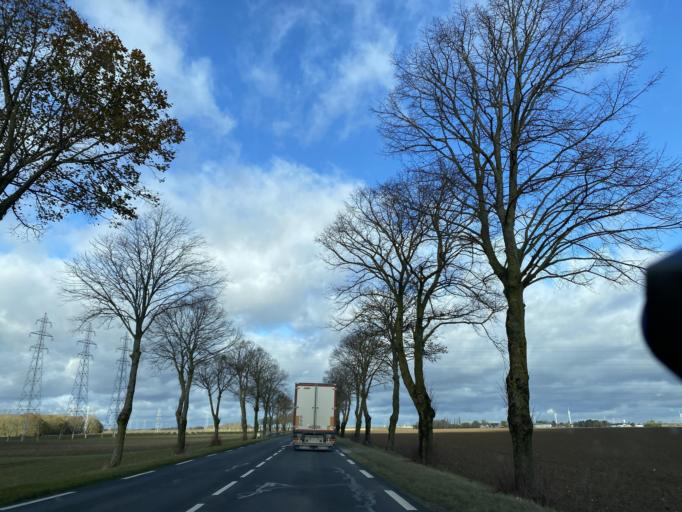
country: FR
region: Centre
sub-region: Departement du Loiret
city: Artenay
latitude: 48.1022
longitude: 1.8646
